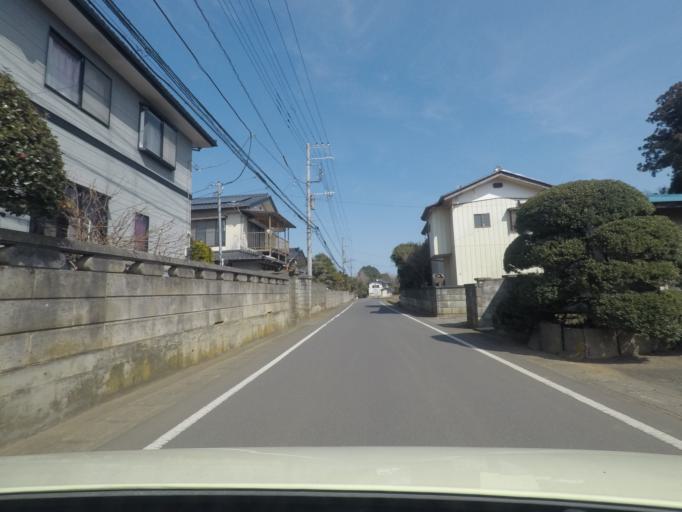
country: JP
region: Ibaraki
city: Okunoya
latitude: 36.2051
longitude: 140.4181
